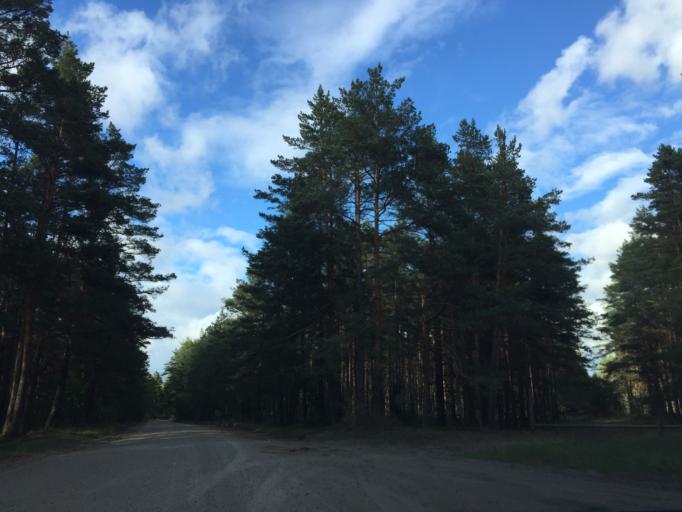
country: LV
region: Adazi
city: Adazi
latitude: 57.1274
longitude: 24.3438
